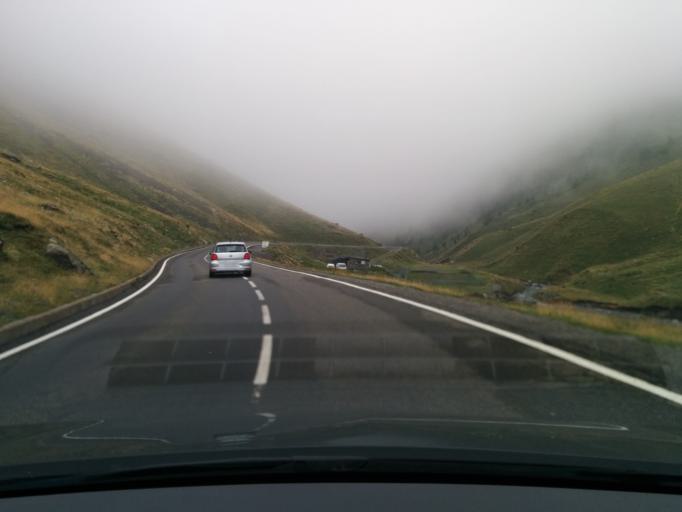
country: ES
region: Aragon
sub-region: Provincia de Huesca
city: Bielsa
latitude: 42.7575
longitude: 0.1945
